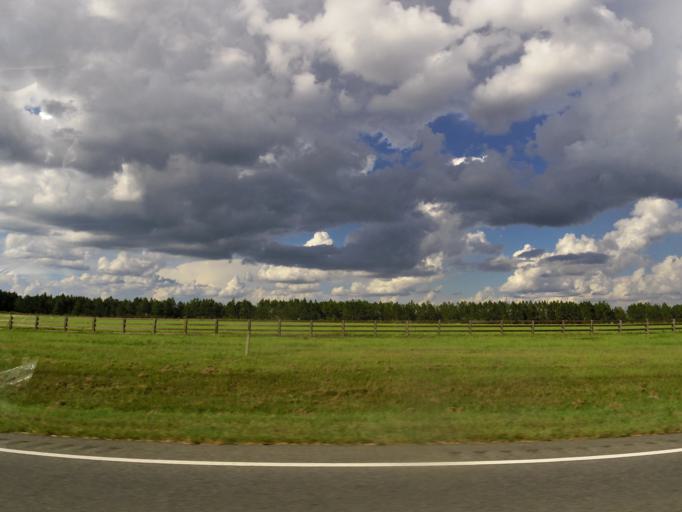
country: US
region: Georgia
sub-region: Lowndes County
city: Remerton
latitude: 30.7998
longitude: -83.3789
